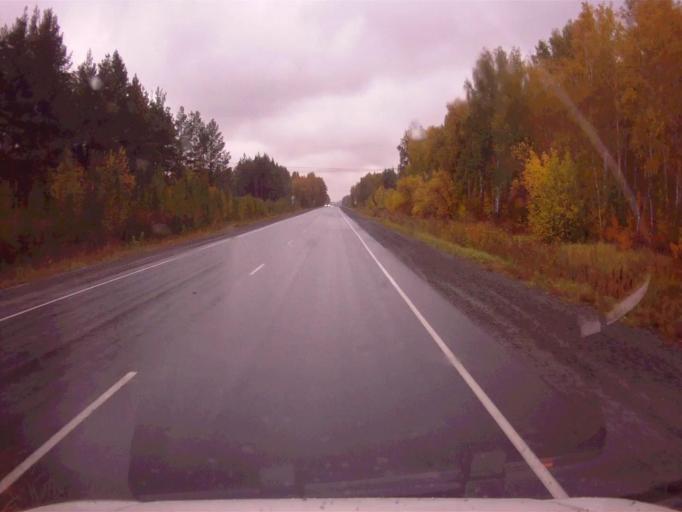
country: RU
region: Chelyabinsk
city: Roshchino
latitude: 55.3807
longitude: 61.1413
